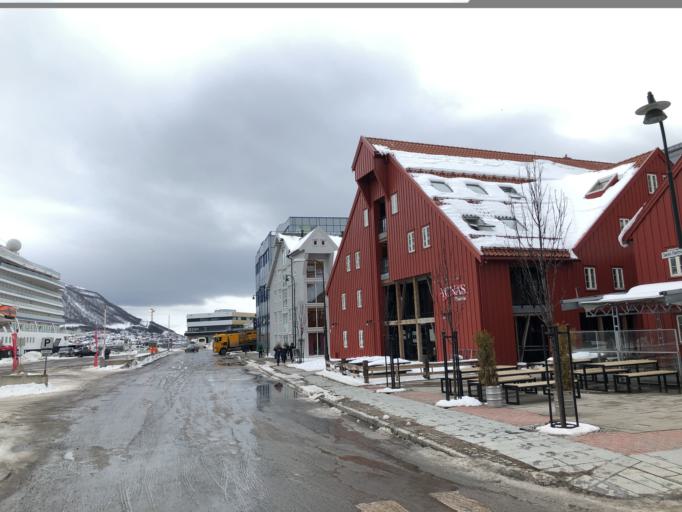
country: NO
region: Troms
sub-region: Tromso
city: Tromso
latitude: 69.6492
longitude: 18.9623
